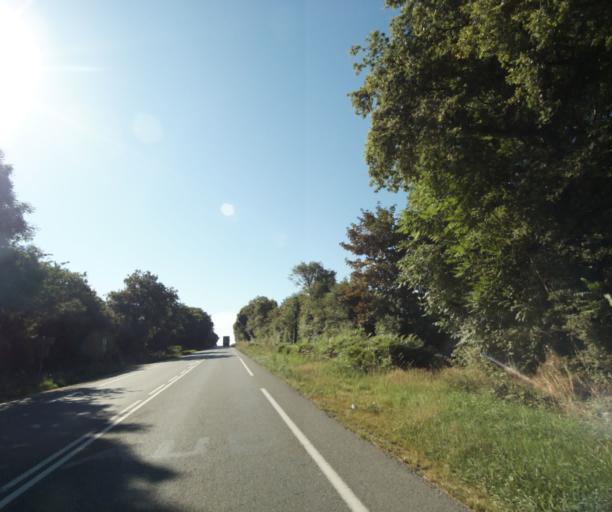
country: FR
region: Pays de la Loire
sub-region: Departement de la Mayenne
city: Bonchamp-les-Laval
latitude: 48.0465
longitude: -0.7288
